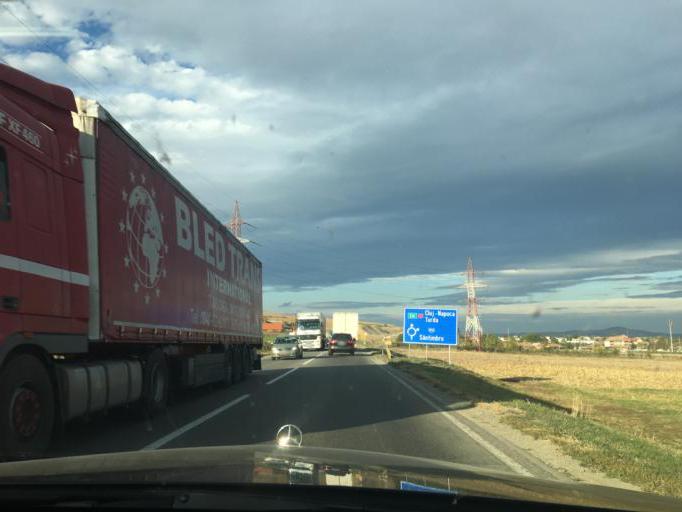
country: RO
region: Alba
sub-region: Comuna Santimbru
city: Santimbru
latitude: 46.1321
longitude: 23.6297
